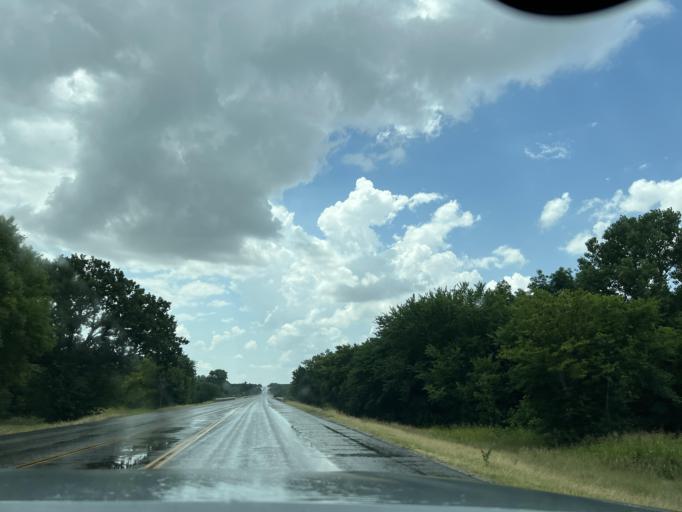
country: US
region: Texas
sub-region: Wise County
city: Boyd
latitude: 33.1070
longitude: -97.6564
